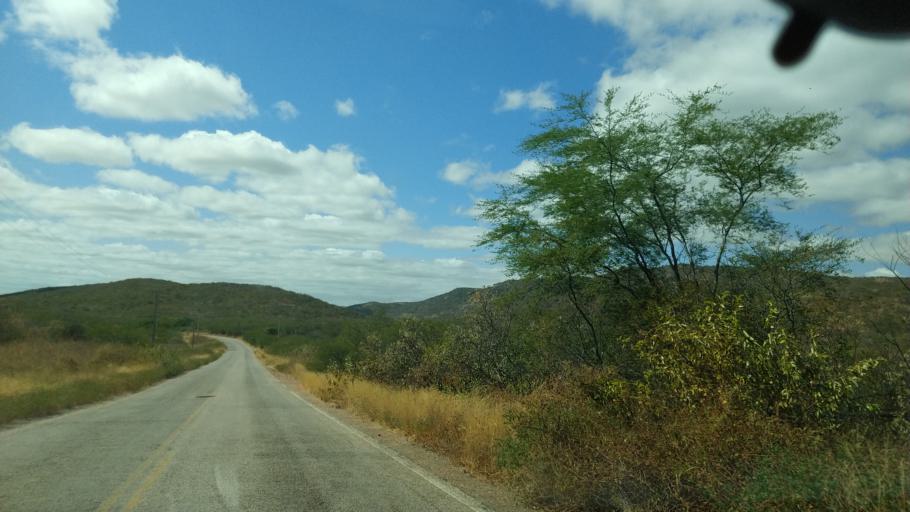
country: BR
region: Rio Grande do Norte
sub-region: Currais Novos
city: Currais Novos
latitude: -6.2641
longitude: -36.5926
